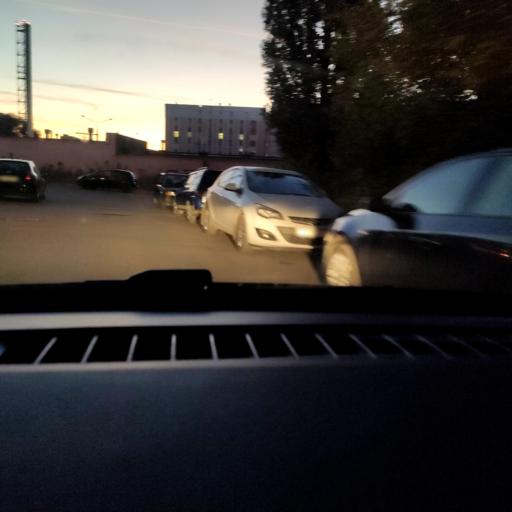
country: RU
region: Voronezj
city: Voronezh
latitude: 51.6451
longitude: 39.1265
